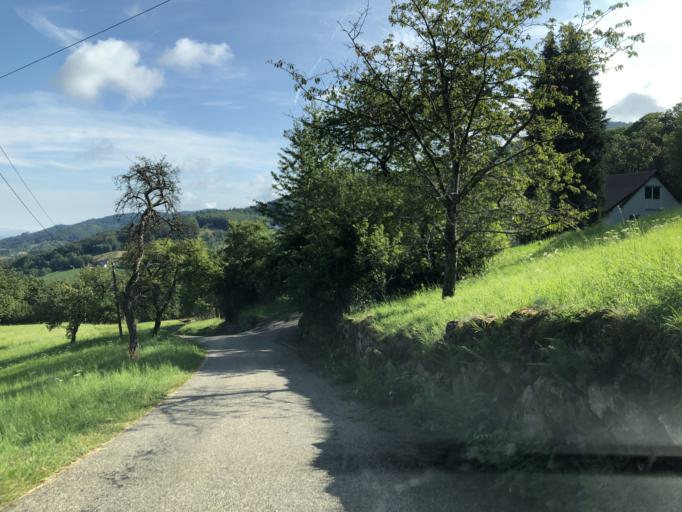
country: DE
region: Baden-Wuerttemberg
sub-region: Freiburg Region
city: Sasbachwalden
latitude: 48.6326
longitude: 8.1451
